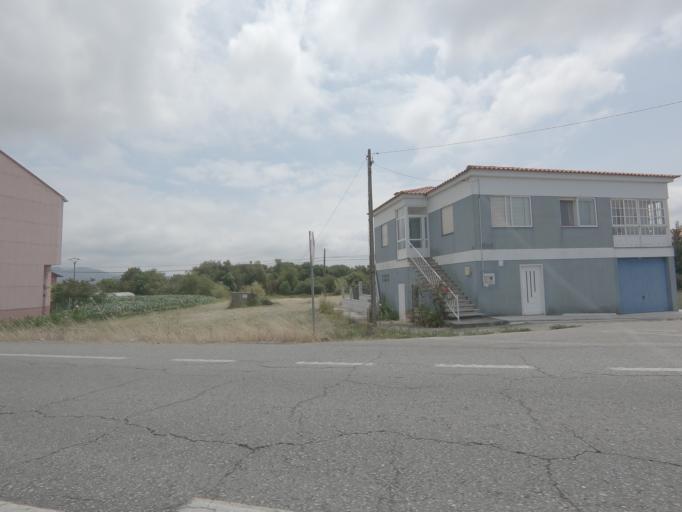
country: ES
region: Galicia
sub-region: Provincia de Pontevedra
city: O Rosal
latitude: 41.9124
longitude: -8.8500
